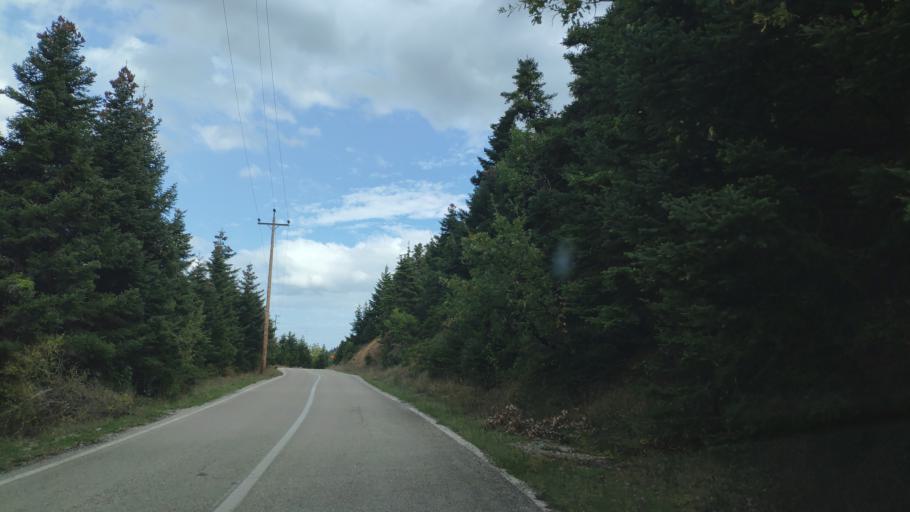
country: GR
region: Central Greece
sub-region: Nomos Fthiotidos
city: Stavros
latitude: 38.7304
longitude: 22.3510
